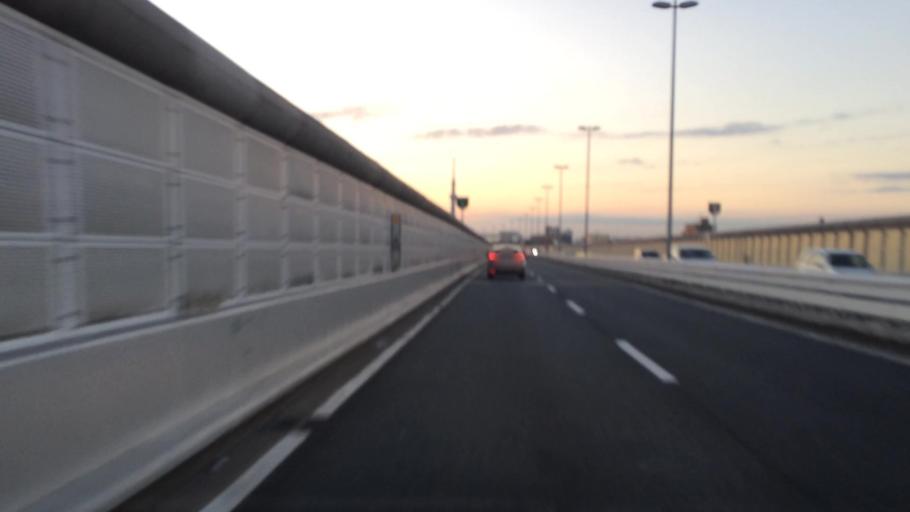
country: JP
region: Tokyo
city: Urayasu
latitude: 35.6981
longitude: 139.8751
